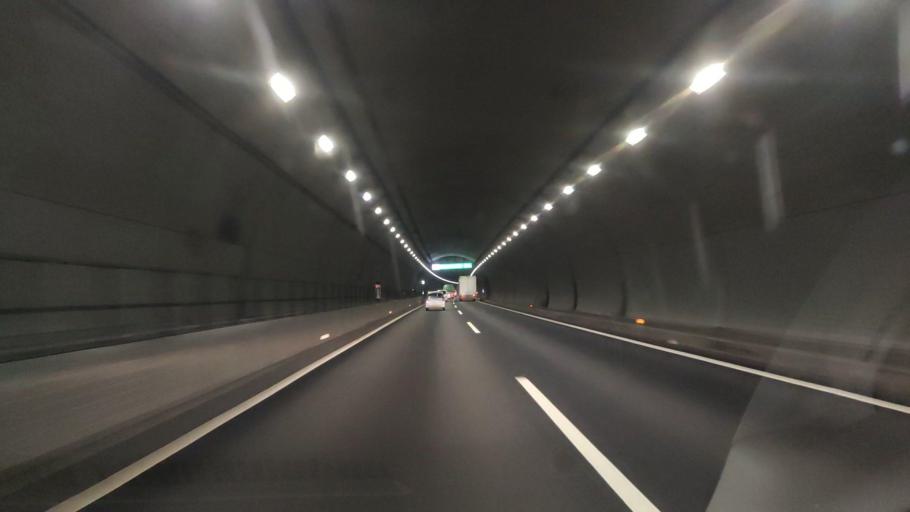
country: JP
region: Kanagawa
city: Zama
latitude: 35.5285
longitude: 139.3427
